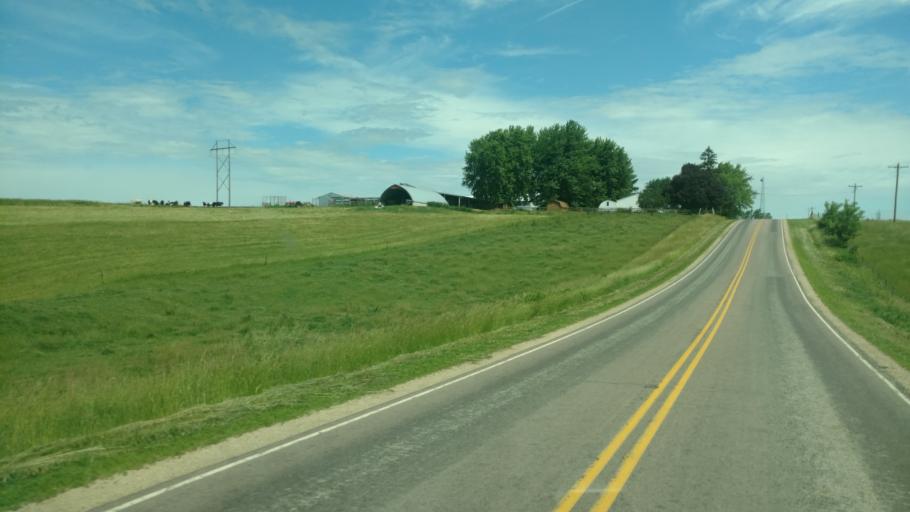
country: US
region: Wisconsin
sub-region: Vernon County
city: Hillsboro
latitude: 43.6623
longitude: -90.4586
